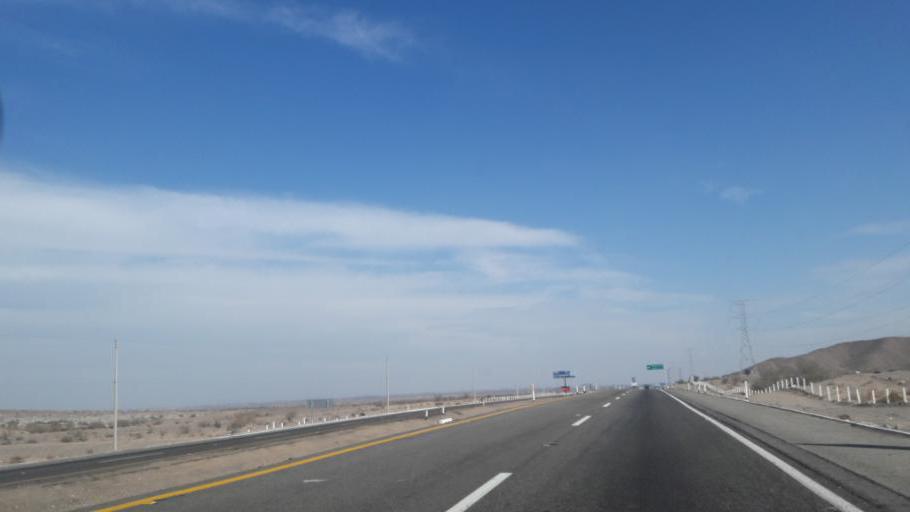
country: MX
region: Baja California
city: Progreso
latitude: 32.5888
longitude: -115.7005
